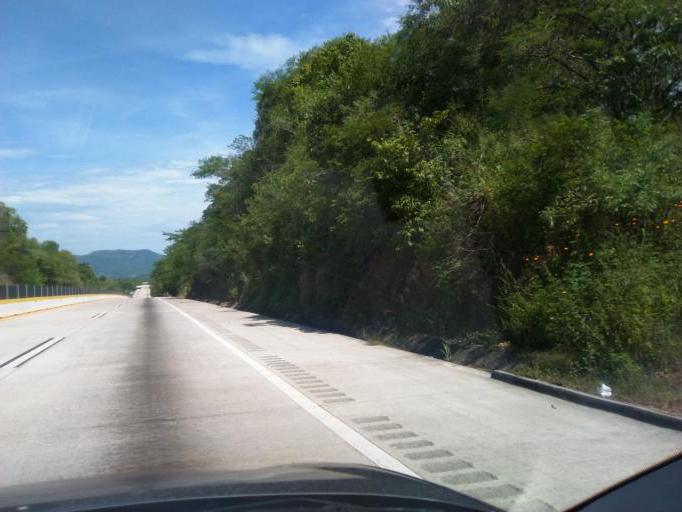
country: MX
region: Guerrero
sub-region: Acapulco de Juarez
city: Kilometro 30
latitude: 16.9639
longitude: -99.7356
